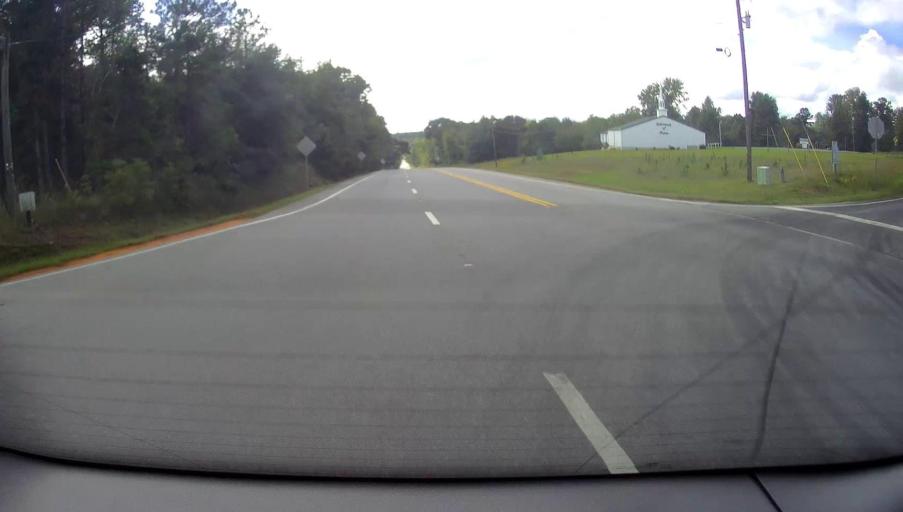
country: US
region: Georgia
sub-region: Baldwin County
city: Milledgeville
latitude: 33.0596
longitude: -83.2769
